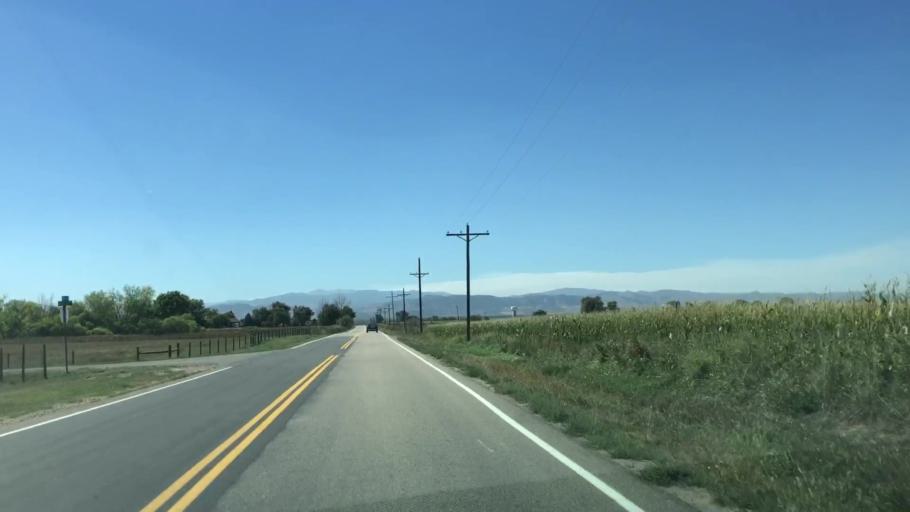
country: US
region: Colorado
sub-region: Weld County
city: Windsor
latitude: 40.5381
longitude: -104.9285
